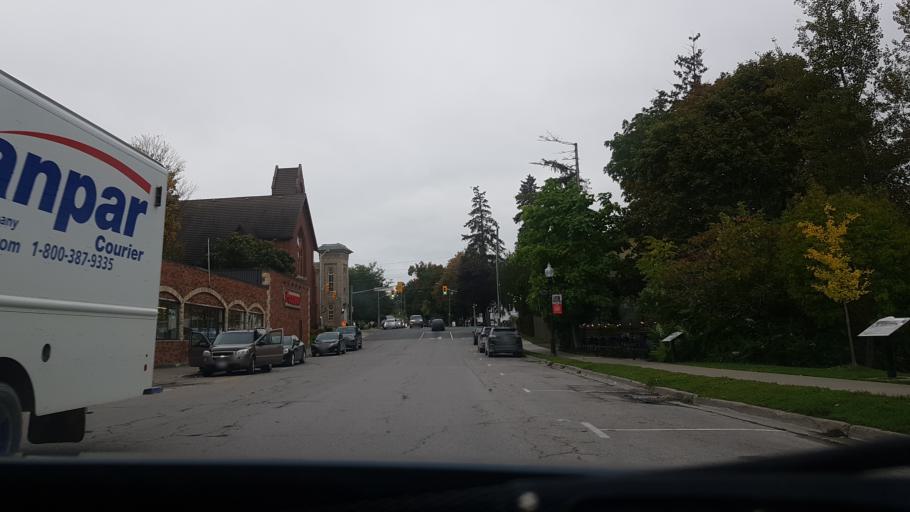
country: CA
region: Ontario
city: Uxbridge
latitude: 44.1041
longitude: -78.9462
